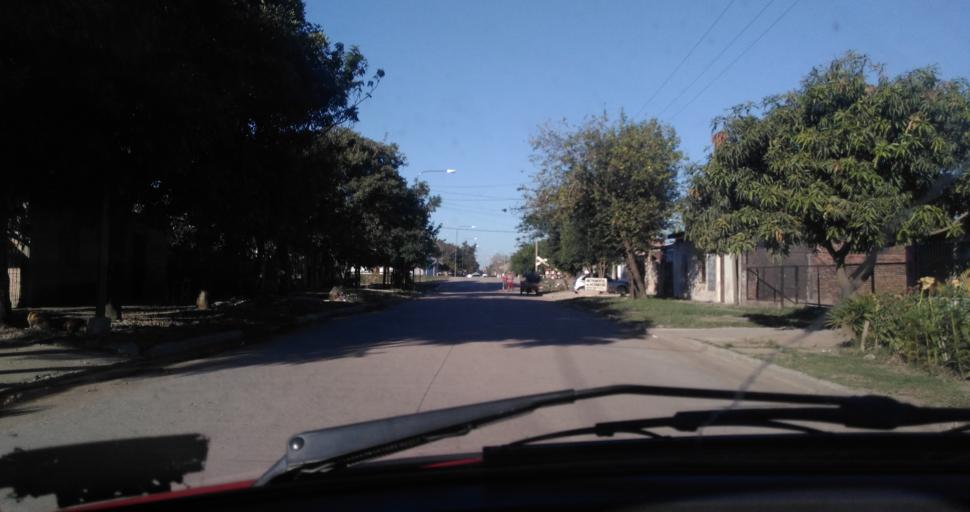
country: AR
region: Chaco
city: Resistencia
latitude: -27.4777
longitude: -58.9667
